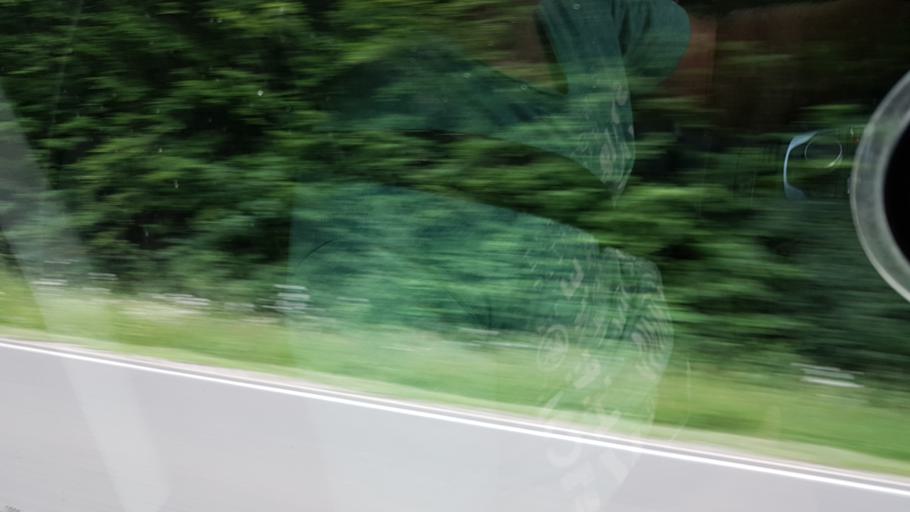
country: DE
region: Rheinland-Pfalz
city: Ulmet
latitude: 49.6092
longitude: 7.4399
